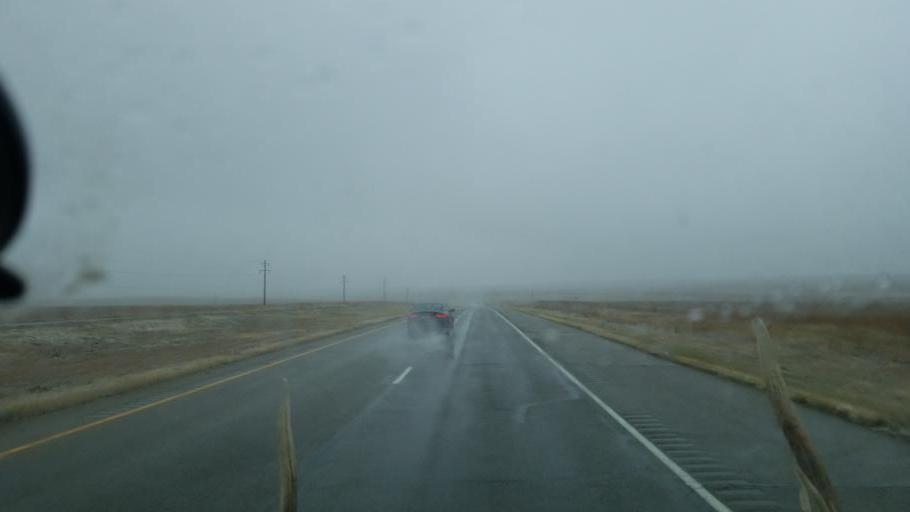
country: US
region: Colorado
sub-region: Pueblo County
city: Colorado City
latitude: 37.8724
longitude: -104.8287
